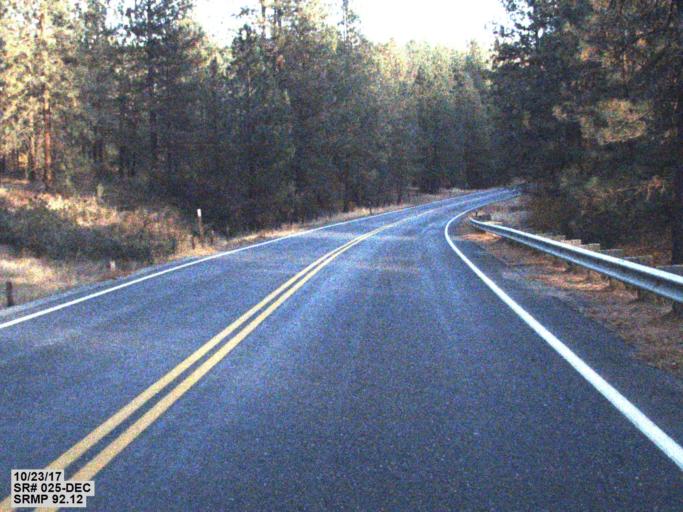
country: US
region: Washington
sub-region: Stevens County
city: Kettle Falls
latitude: 48.7238
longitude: -118.0366
